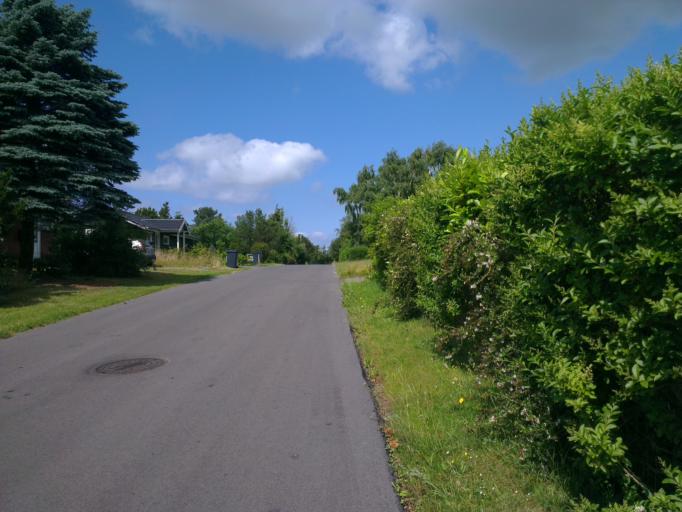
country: DK
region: Zealand
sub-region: Lejre Kommune
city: Ejby
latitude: 55.7456
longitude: 11.8665
